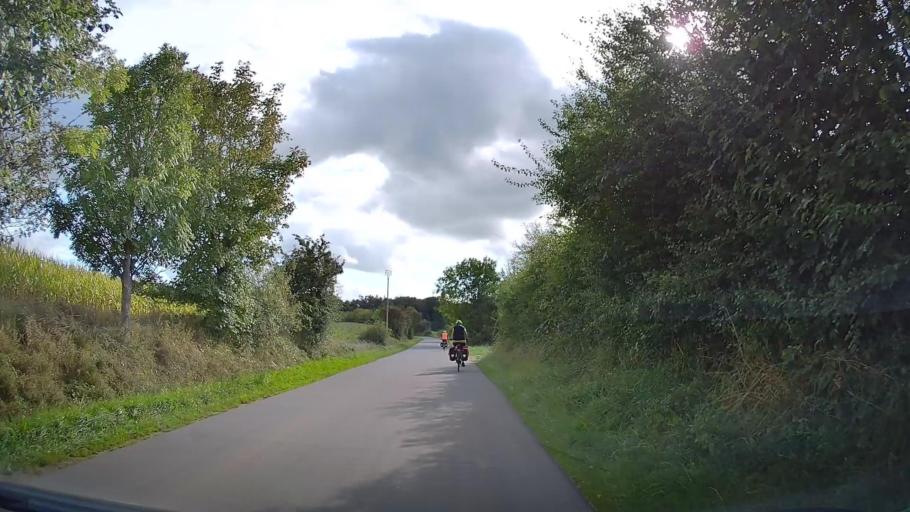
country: DE
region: Schleswig-Holstein
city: Steinberg
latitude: 54.7902
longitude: 9.7795
